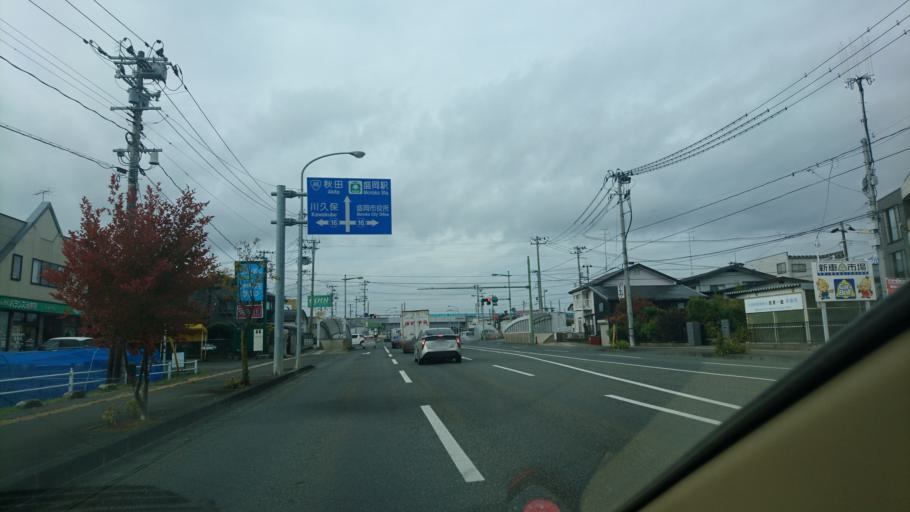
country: JP
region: Iwate
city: Morioka-shi
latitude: 39.6846
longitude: 141.1521
